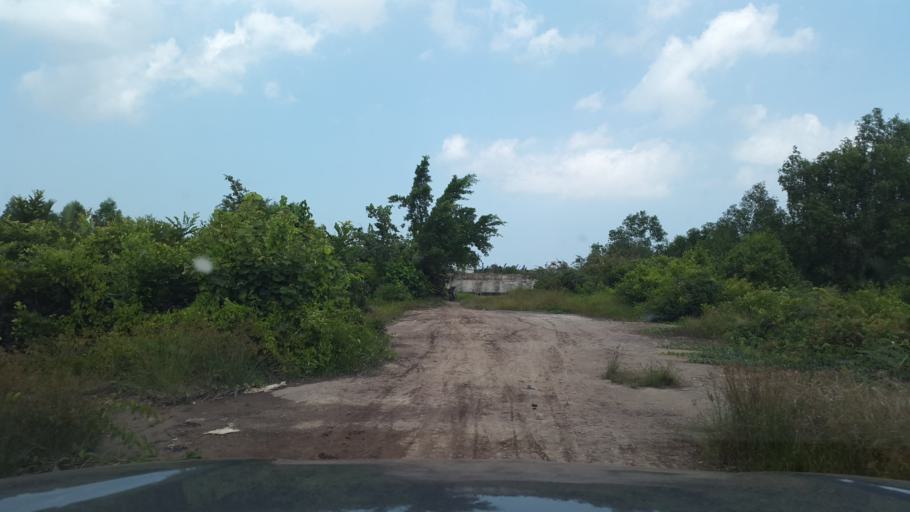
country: ID
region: South Sumatra
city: Sungsang
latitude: -2.3610
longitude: 104.8875
